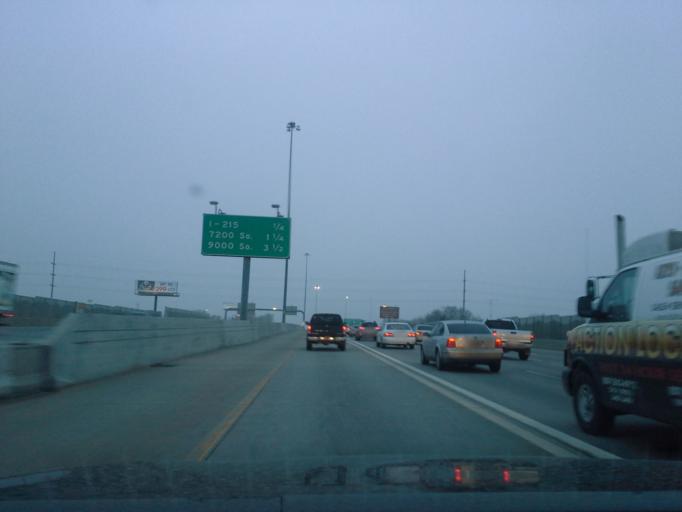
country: US
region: Utah
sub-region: Salt Lake County
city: Murray
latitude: 40.6447
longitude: -111.9028
